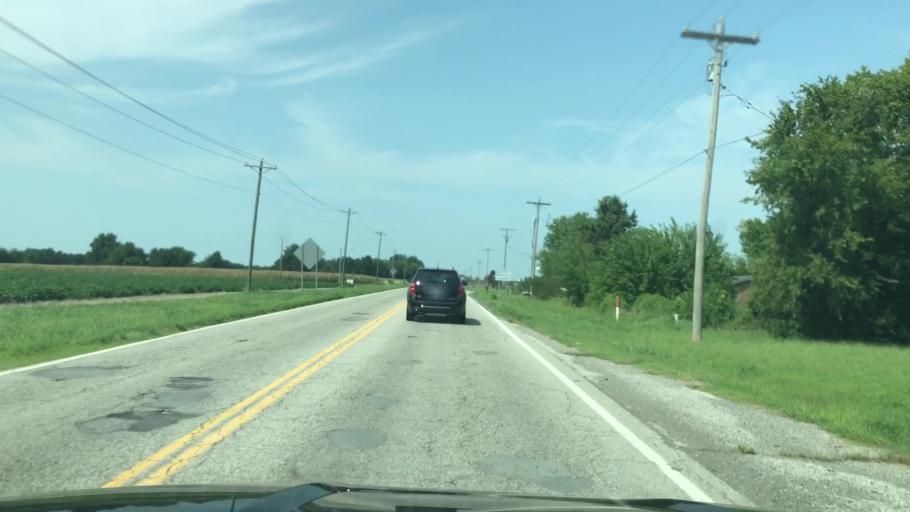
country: US
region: Oklahoma
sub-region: Ottawa County
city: Miami
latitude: 36.8986
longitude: -94.8419
